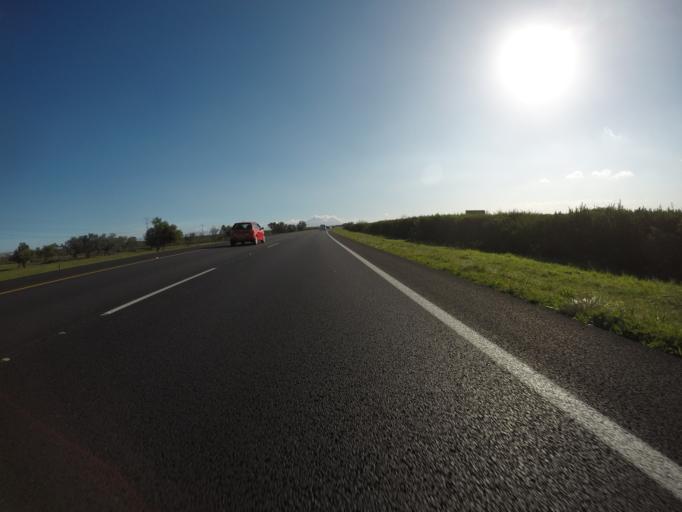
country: ZA
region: Western Cape
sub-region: Cape Winelands District Municipality
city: Stellenbosch
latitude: -34.0426
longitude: 18.7321
